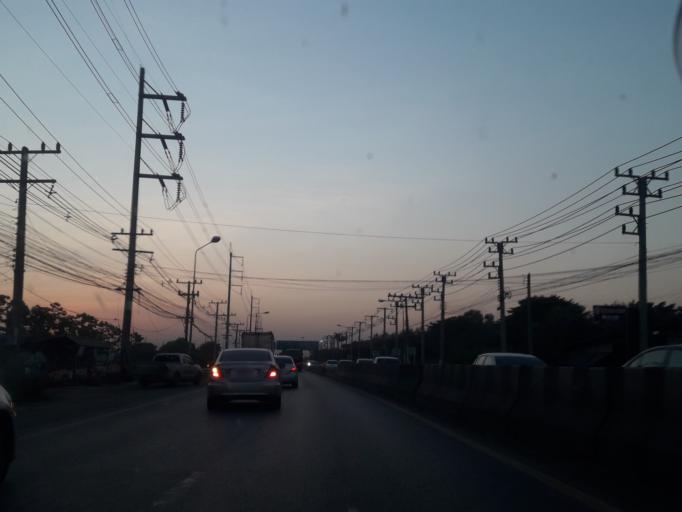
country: TH
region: Pathum Thani
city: Thanyaburi
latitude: 14.0671
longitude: 100.7026
